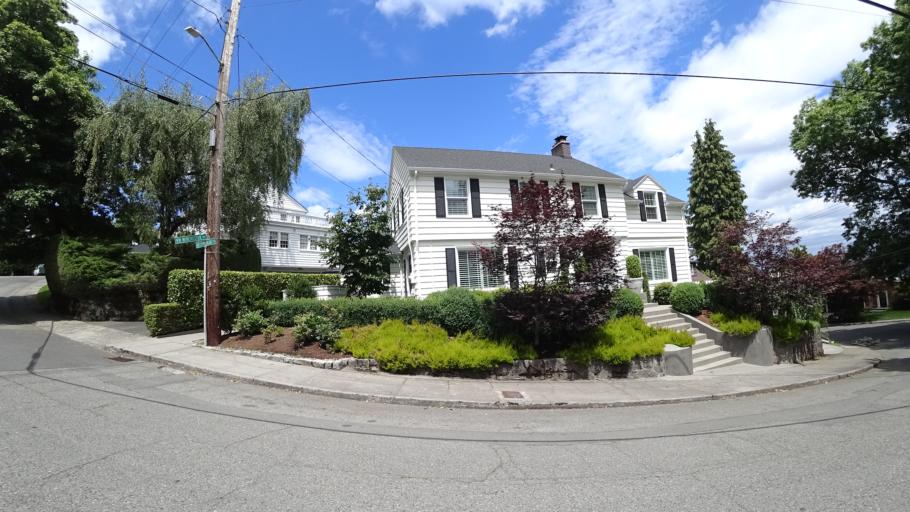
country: US
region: Oregon
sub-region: Multnomah County
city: Portland
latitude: 45.5287
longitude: -122.7101
